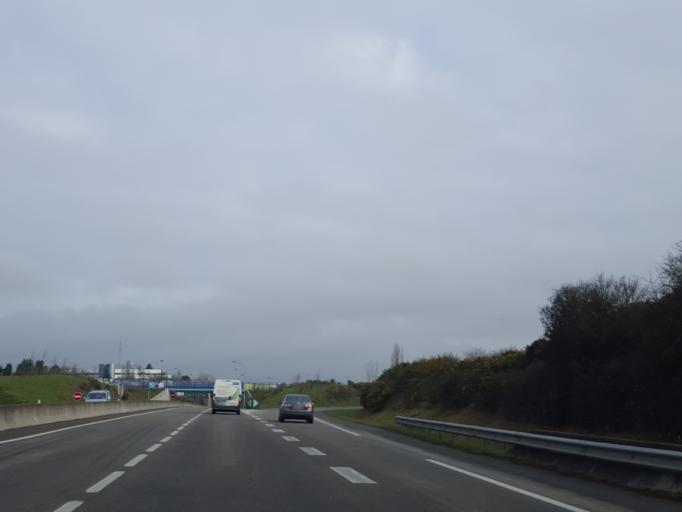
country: FR
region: Pays de la Loire
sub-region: Departement de la Vendee
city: La Roche-sur-Yon
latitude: 46.6793
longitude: -1.4518
